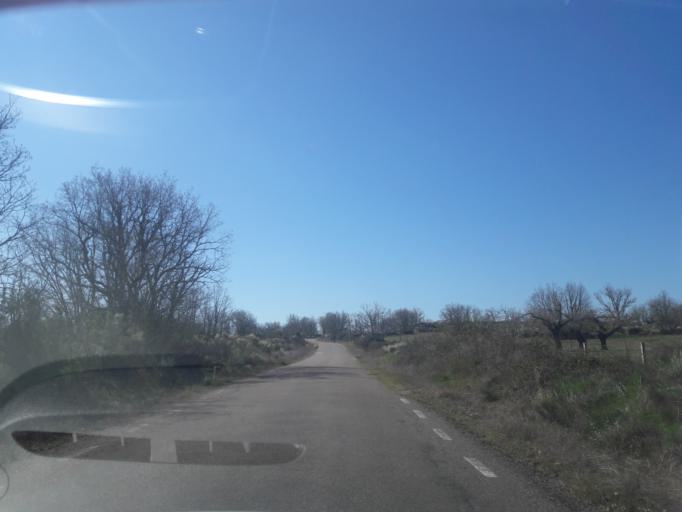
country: ES
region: Castille and Leon
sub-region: Provincia de Salamanca
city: Valsalabroso
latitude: 41.1296
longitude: -6.4824
